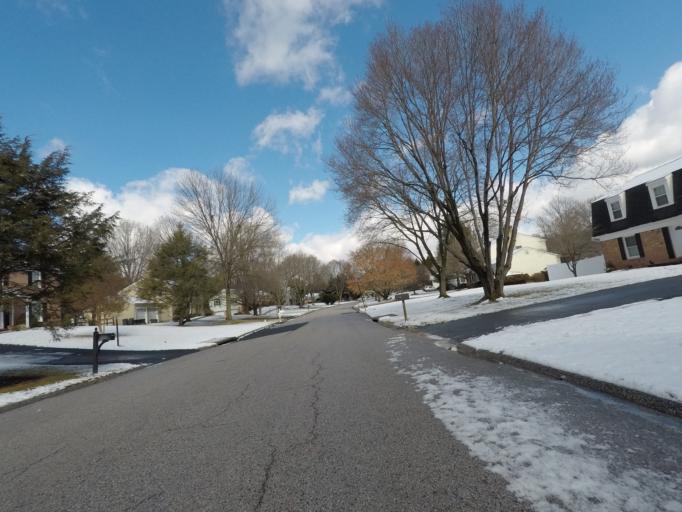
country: US
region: Maryland
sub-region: Howard County
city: Columbia
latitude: 39.2657
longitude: -76.8384
